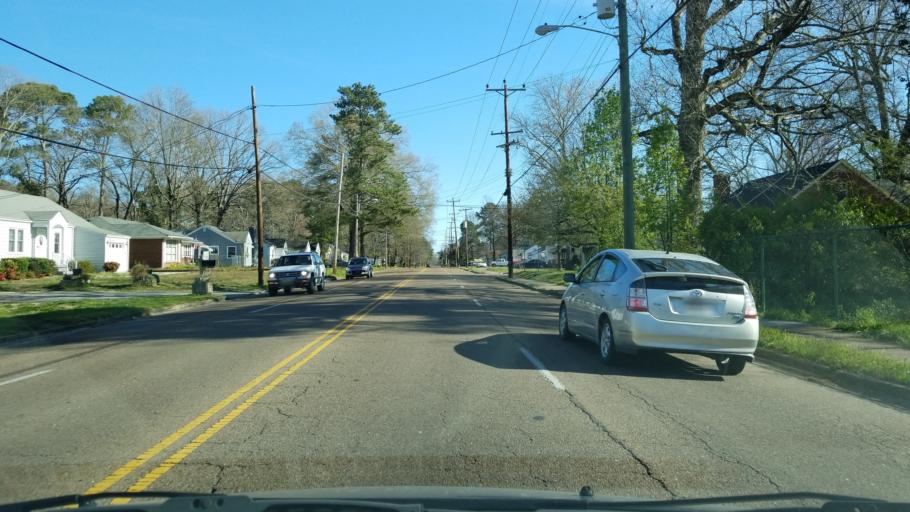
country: US
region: Tennessee
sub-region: Hamilton County
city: East Ridge
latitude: 35.0197
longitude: -85.2246
